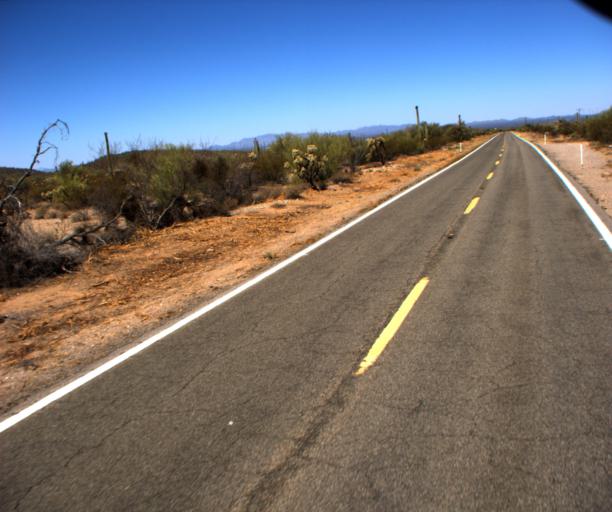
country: US
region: Arizona
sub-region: Pima County
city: Sells
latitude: 32.1771
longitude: -112.2485
